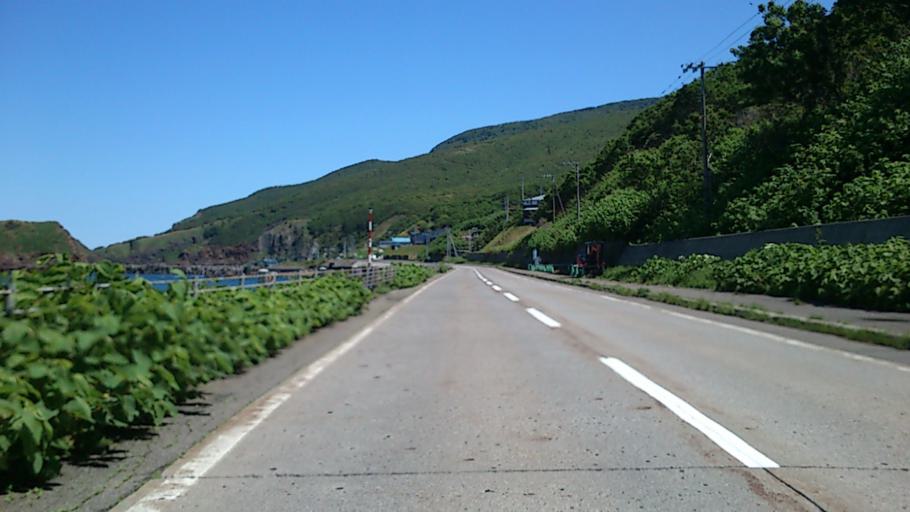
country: JP
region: Hokkaido
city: Rumoi
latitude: 43.7714
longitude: 141.3665
